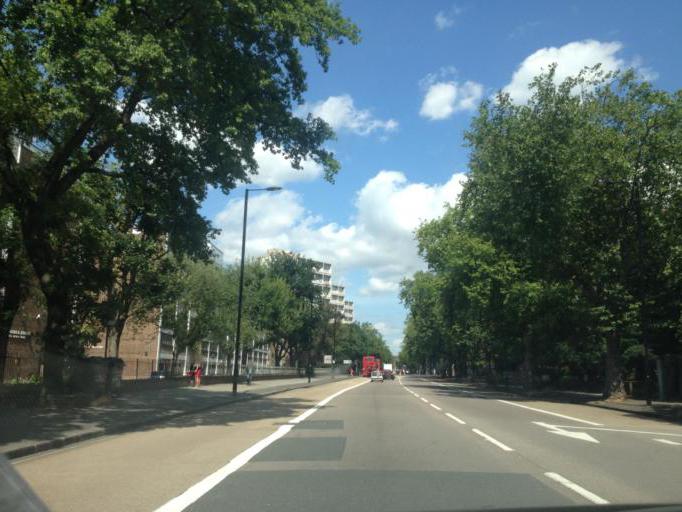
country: GB
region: England
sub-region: Greater London
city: Bayswater
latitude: 51.5292
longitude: -0.1825
